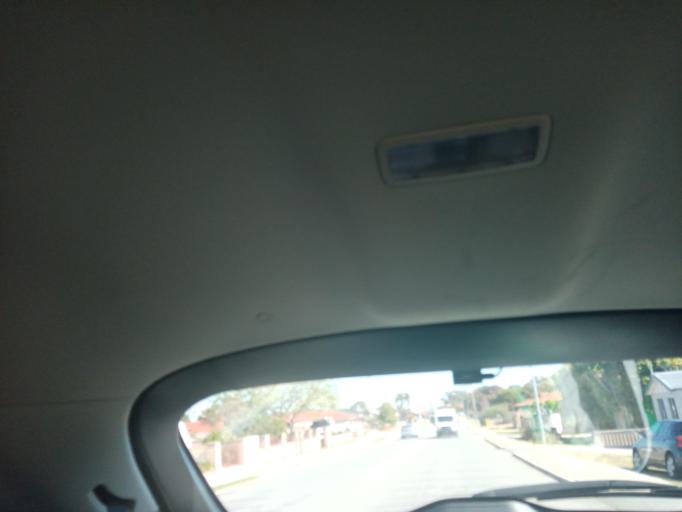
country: AU
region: Western Australia
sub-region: City of Cockburn
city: Spearwood
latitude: -32.1177
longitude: 115.7827
